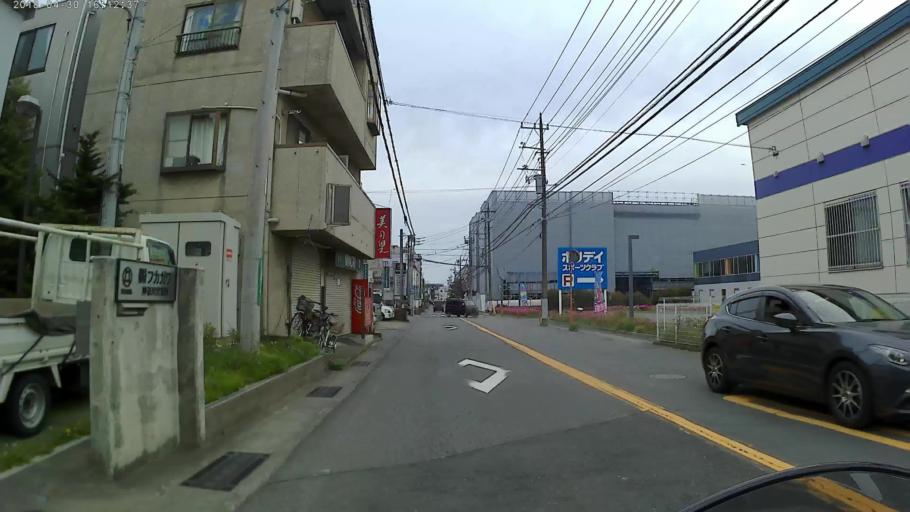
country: JP
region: Kanagawa
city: Minami-rinkan
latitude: 35.4949
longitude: 139.4298
